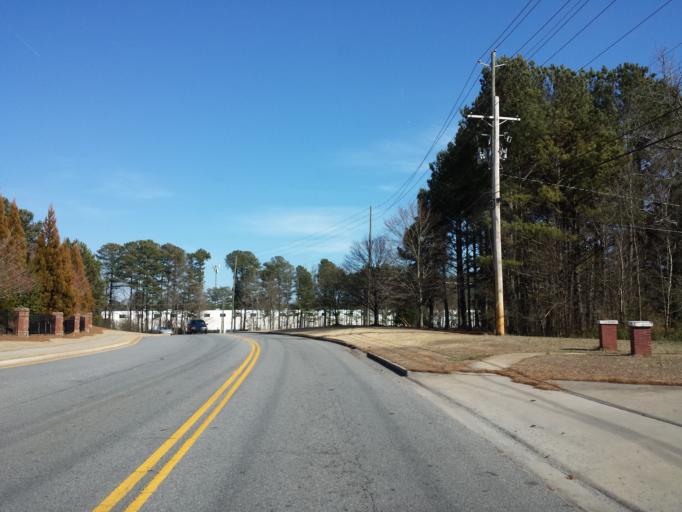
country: US
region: Georgia
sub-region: Cobb County
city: Kennesaw
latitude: 34.0287
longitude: -84.5920
